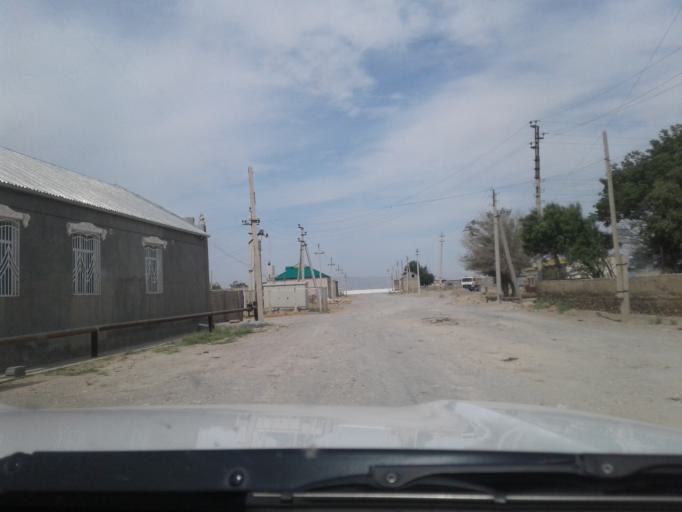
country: TM
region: Balkan
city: Serdar
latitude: 38.9917
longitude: 56.2731
